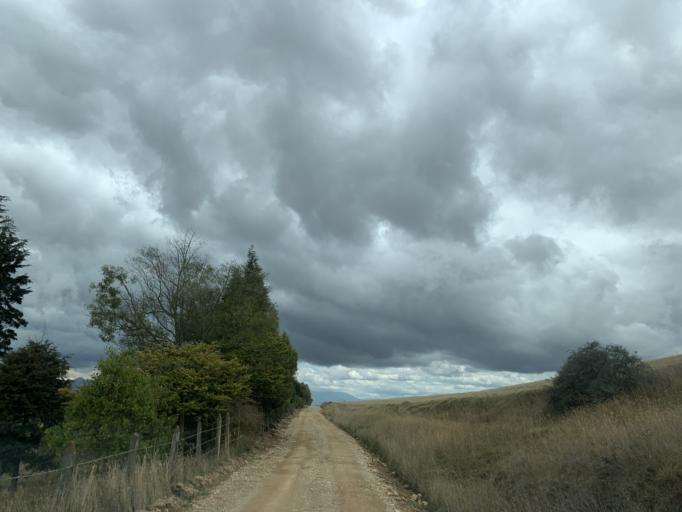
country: CO
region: Boyaca
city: Tunja
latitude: 5.5586
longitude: -73.3141
